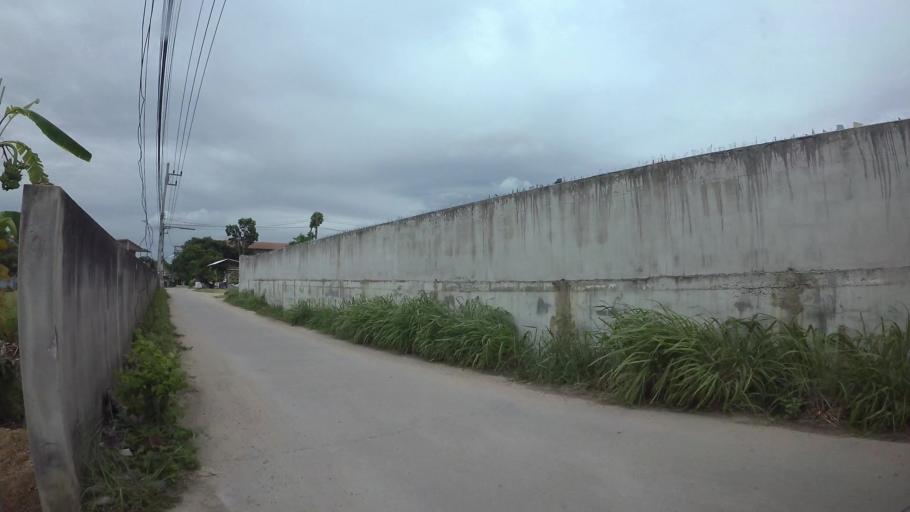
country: TH
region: Chon Buri
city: Si Racha
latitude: 13.1576
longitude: 100.9758
